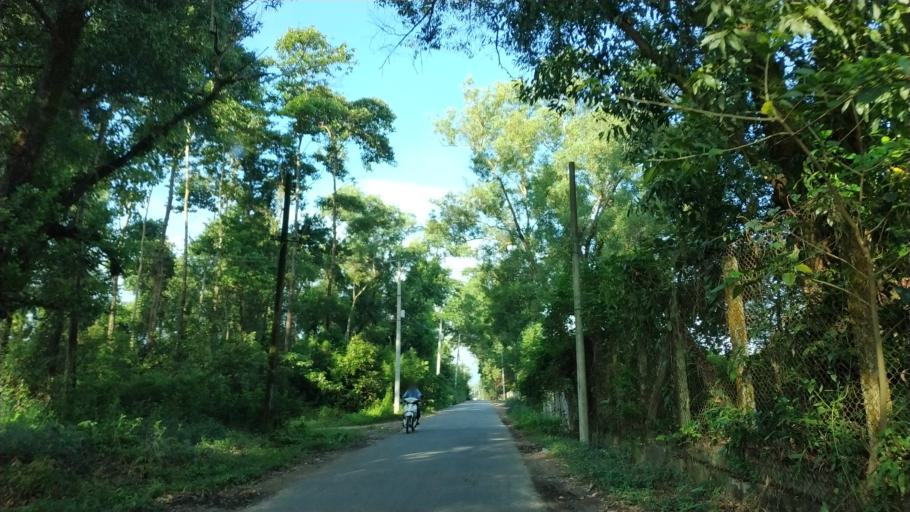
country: MM
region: Tanintharyi
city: Dawei
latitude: 14.0994
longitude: 98.2023
